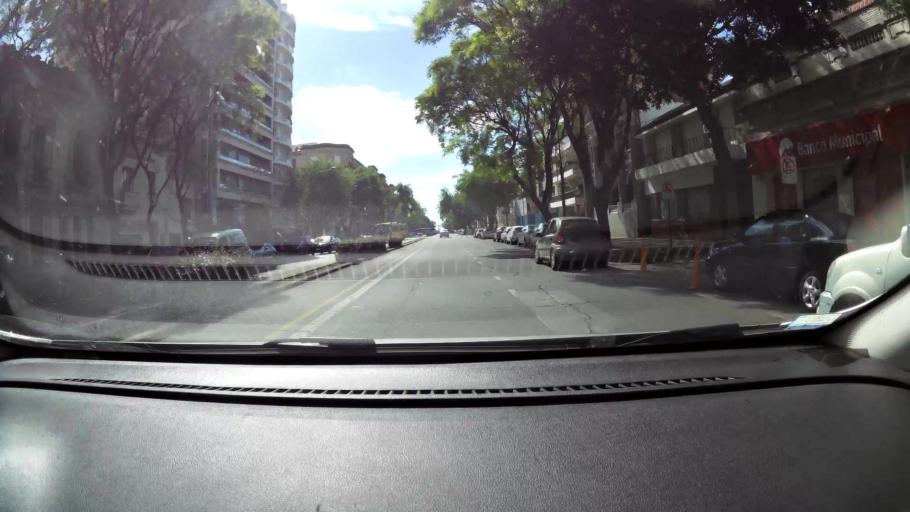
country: AR
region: Santa Fe
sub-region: Departamento de Rosario
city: Rosario
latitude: -32.9593
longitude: -60.6306
